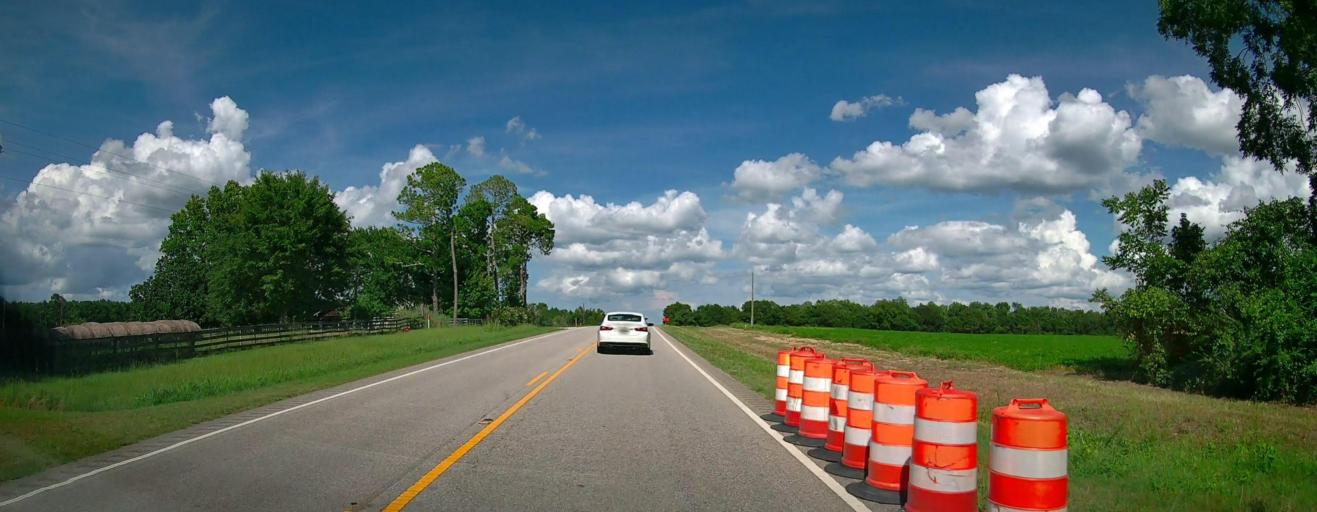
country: US
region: Alabama
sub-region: Lee County
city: Auburn
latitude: 32.4286
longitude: -85.4392
